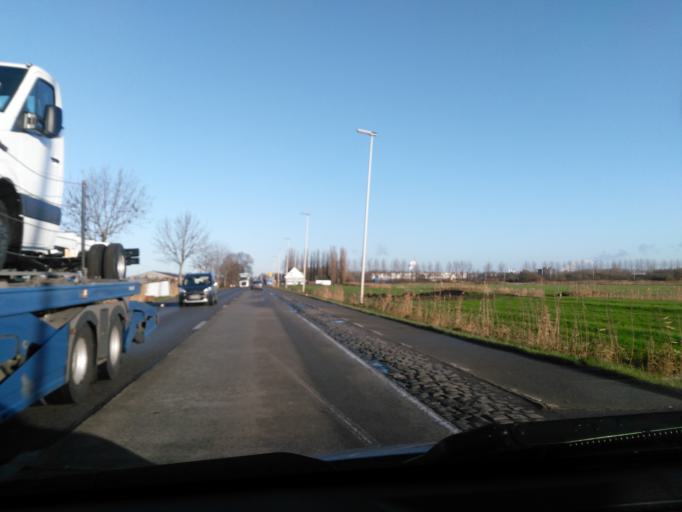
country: BE
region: Flanders
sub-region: Provincie Oost-Vlaanderen
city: Sint-Gillis-Waas
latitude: 51.2433
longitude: 4.1899
